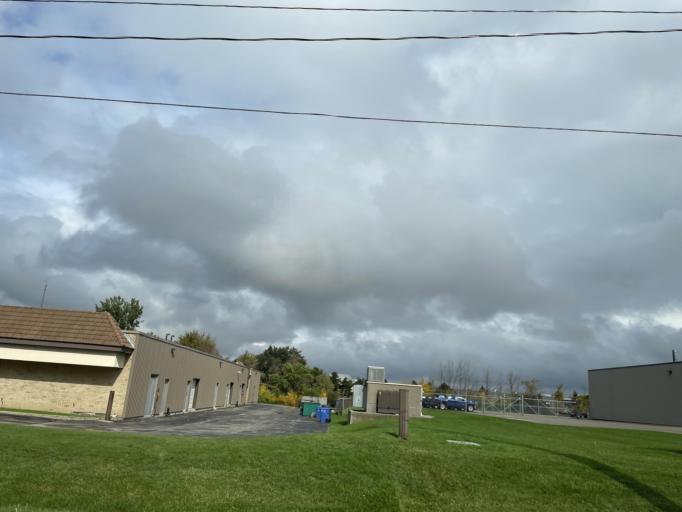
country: CA
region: Ontario
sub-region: Wellington County
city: Guelph
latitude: 43.5334
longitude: -80.3184
